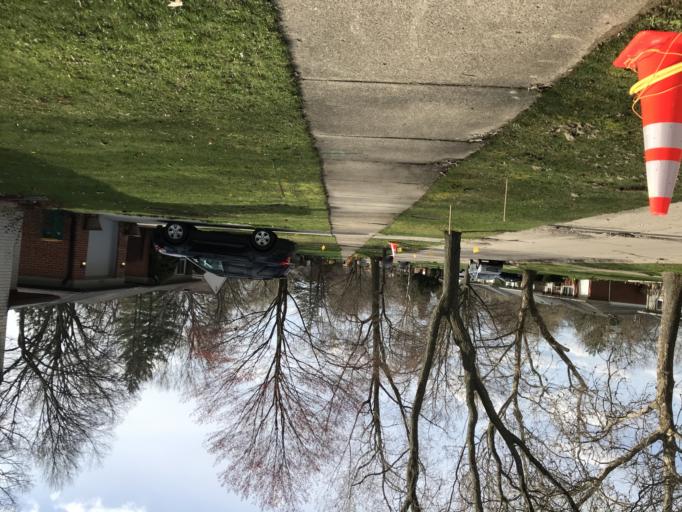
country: US
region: Michigan
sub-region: Oakland County
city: Farmington
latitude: 42.4619
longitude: -83.3472
